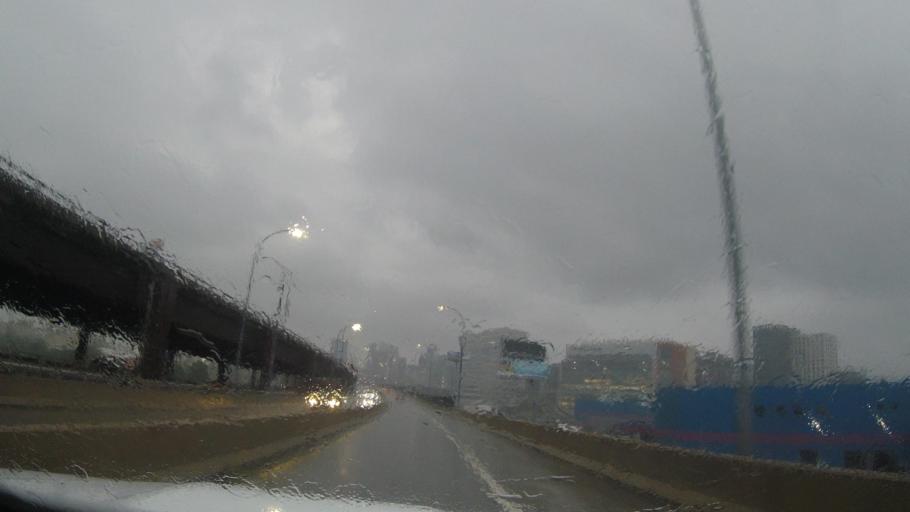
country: US
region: Massachusetts
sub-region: Suffolk County
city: Boston
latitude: 42.3771
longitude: -71.0753
